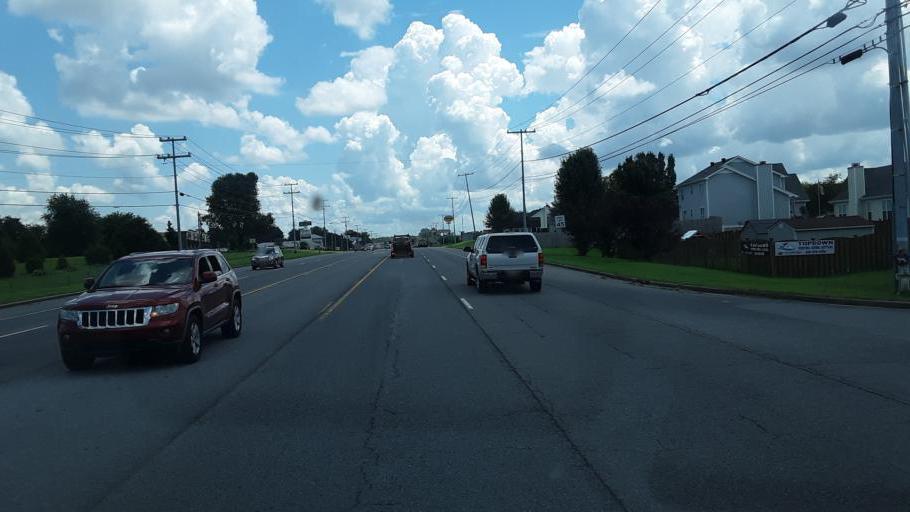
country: US
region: Tennessee
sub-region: Montgomery County
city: Clarksville
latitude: 36.6265
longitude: -87.3290
